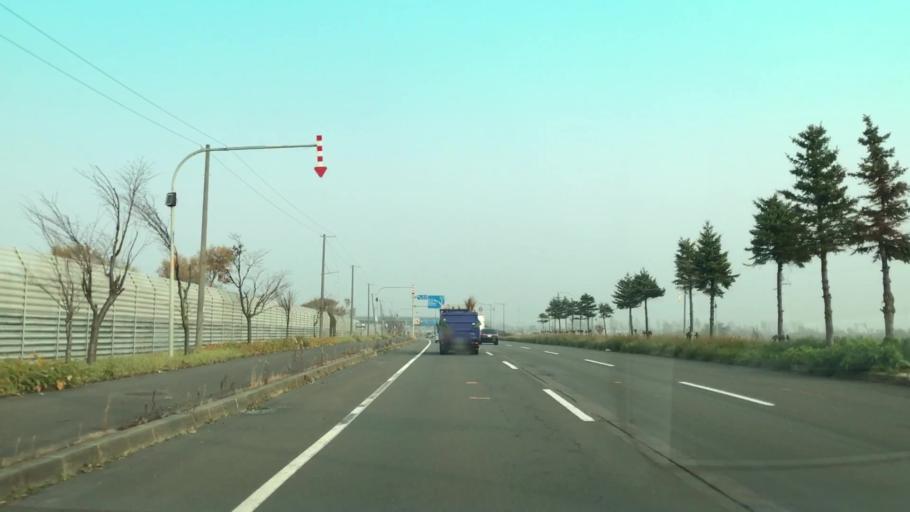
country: JP
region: Hokkaido
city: Ishikari
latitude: 43.1751
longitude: 141.3483
